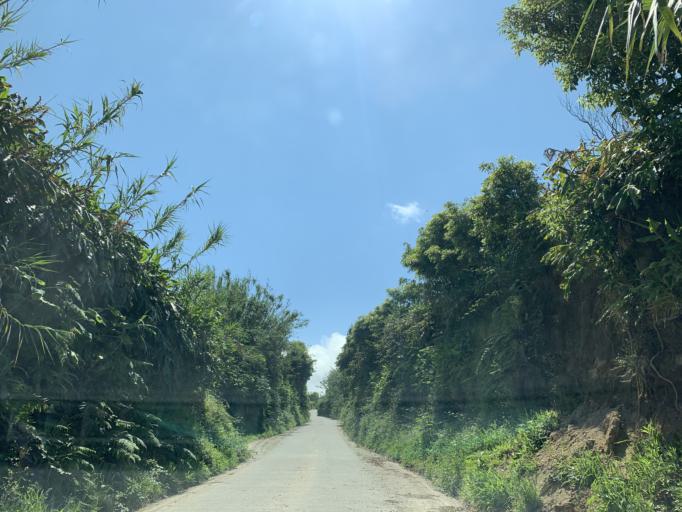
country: PT
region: Azores
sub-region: Ponta Delgada
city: Arrifes
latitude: 37.8635
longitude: -25.7139
